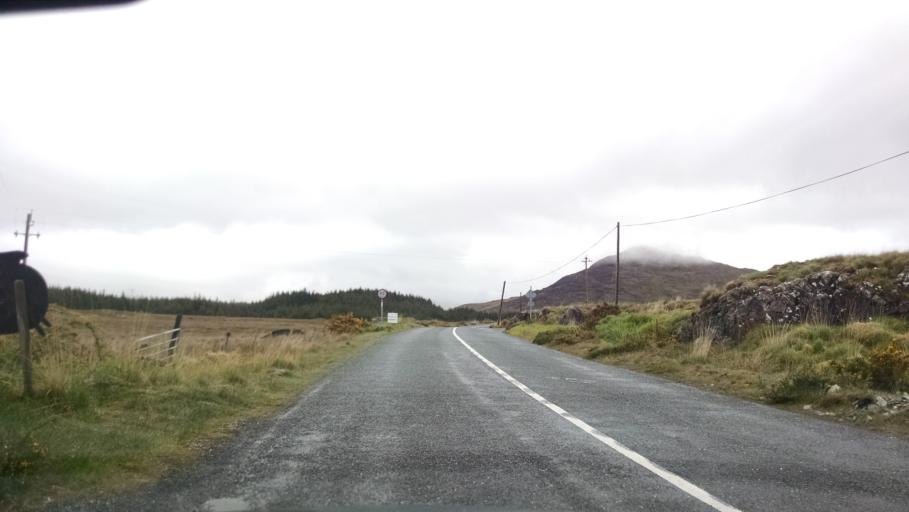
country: IE
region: Connaught
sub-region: County Galway
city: Clifden
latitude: 53.4665
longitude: -9.7538
